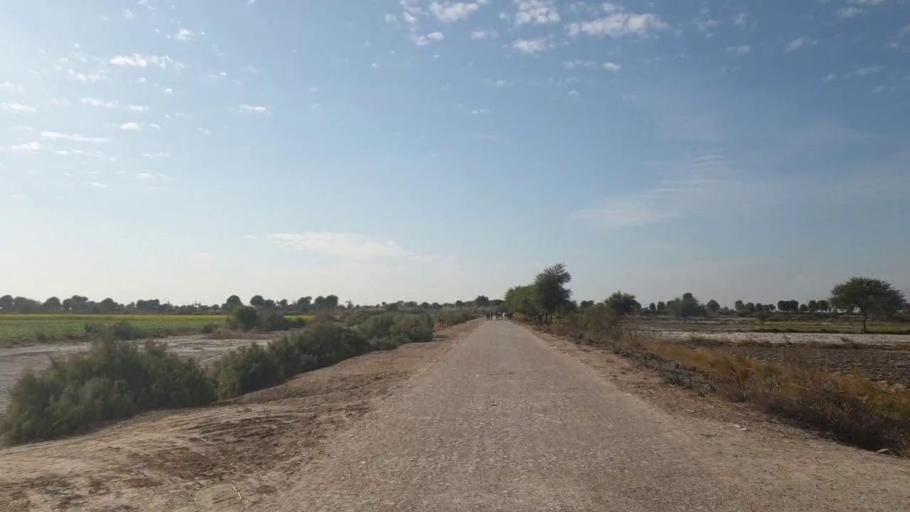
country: PK
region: Sindh
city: Sanghar
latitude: 26.0739
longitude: 68.8761
